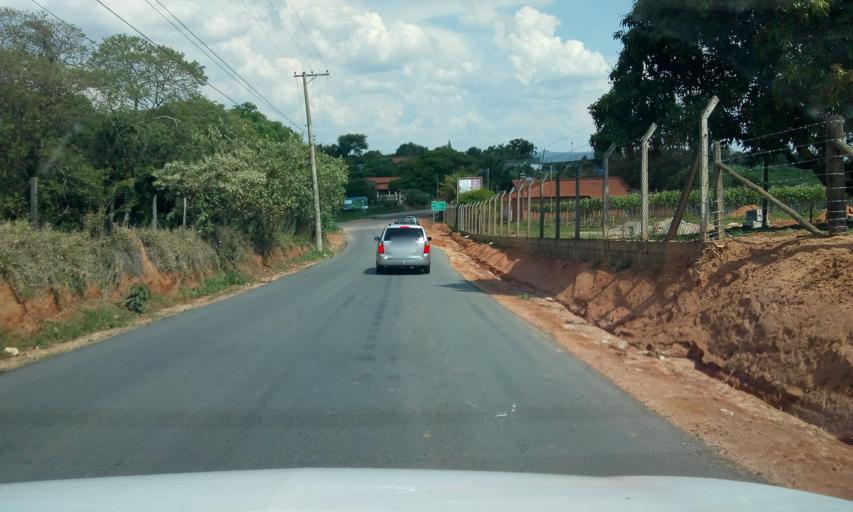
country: BR
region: Sao Paulo
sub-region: Itupeva
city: Itupeva
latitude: -23.1248
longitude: -47.0047
